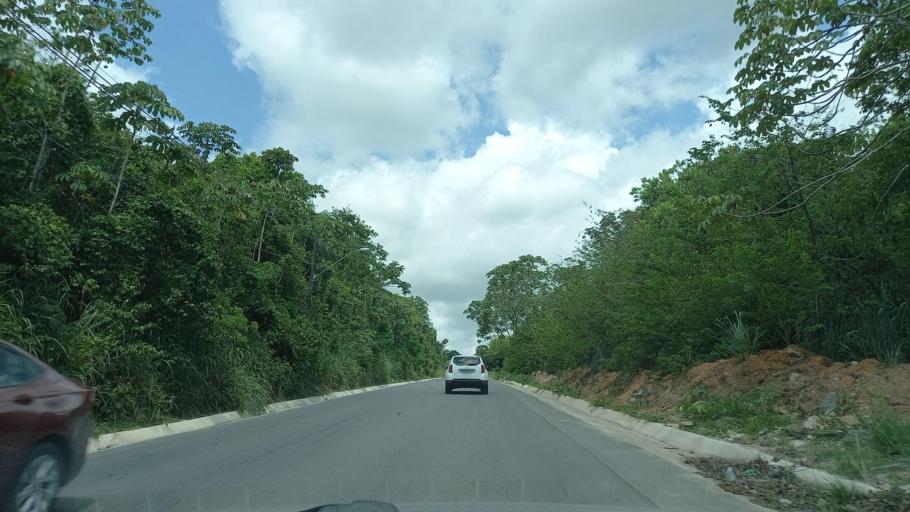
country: BR
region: Pernambuco
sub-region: Jaboatao Dos Guararapes
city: Jaboatao
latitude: -8.1590
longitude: -34.9948
